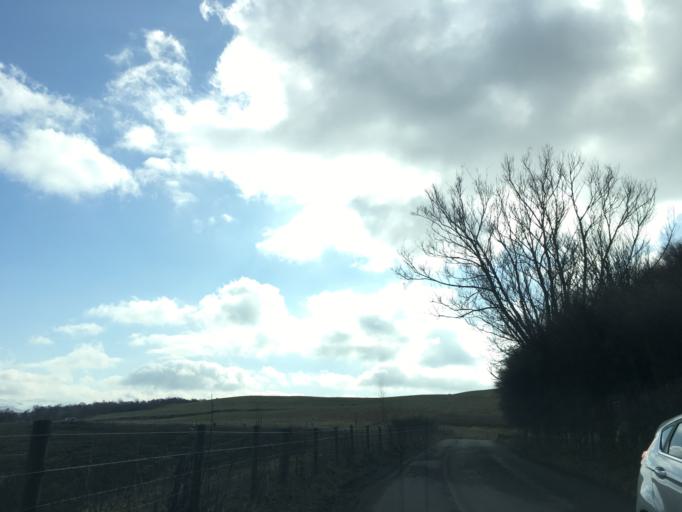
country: GB
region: Scotland
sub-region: Highland
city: Kingussie
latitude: 57.0707
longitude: -4.0439
